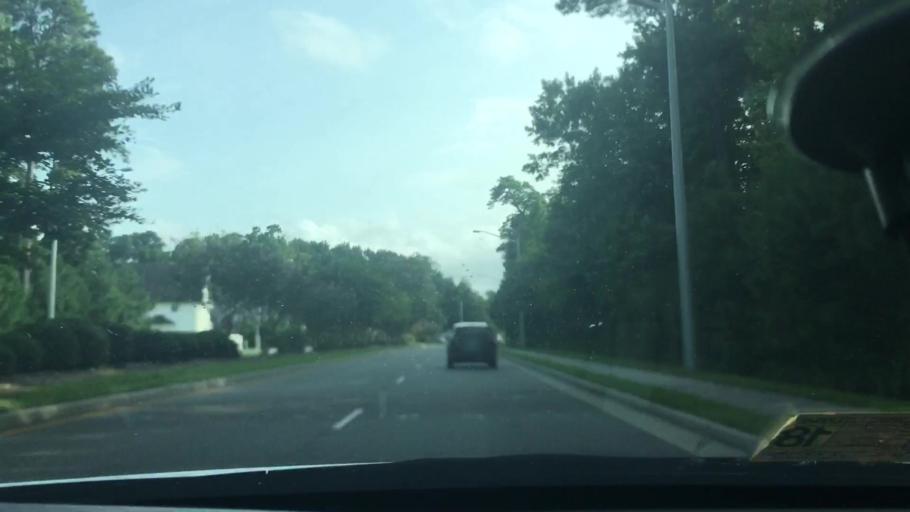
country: US
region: Virginia
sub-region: City of Virginia Beach
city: Virginia Beach
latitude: 36.8262
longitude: -75.9979
